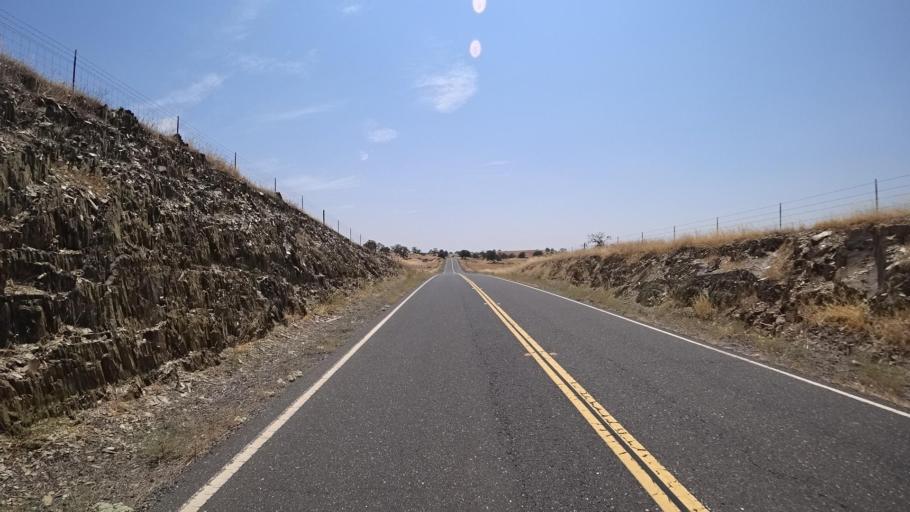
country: US
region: California
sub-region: Tuolumne County
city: Jamestown
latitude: 37.6345
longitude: -120.3714
